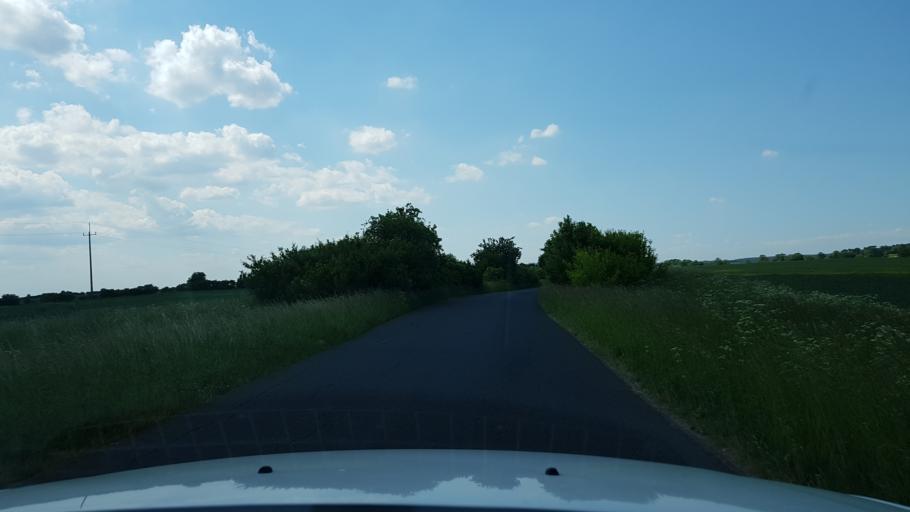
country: PL
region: West Pomeranian Voivodeship
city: Trzcinsko Zdroj
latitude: 52.9923
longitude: 14.5871
